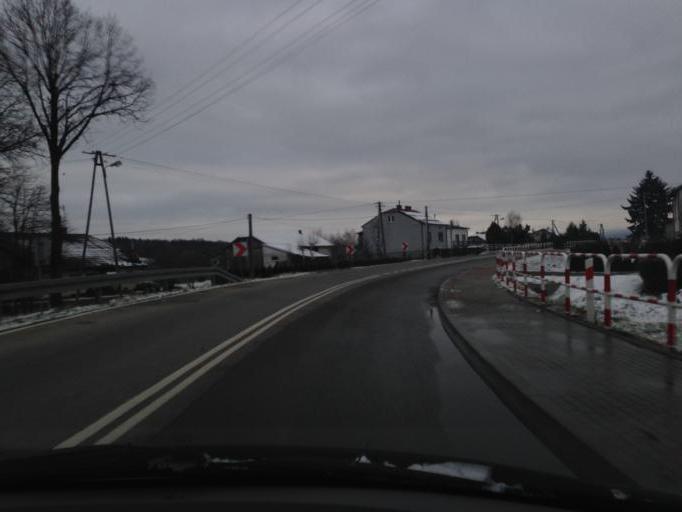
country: PL
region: Lesser Poland Voivodeship
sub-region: Powiat gorlicki
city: Moszczenica
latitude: 49.7057
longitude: 21.1354
